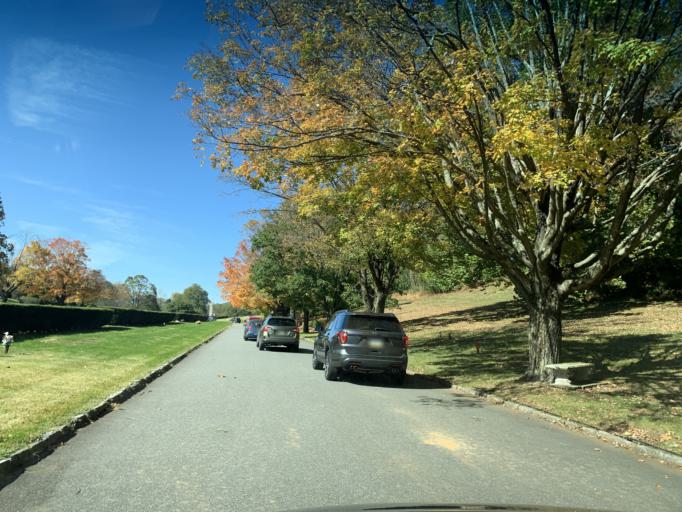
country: US
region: Pennsylvania
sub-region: Berks County
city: Reiffton
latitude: 40.3119
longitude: -75.8862
